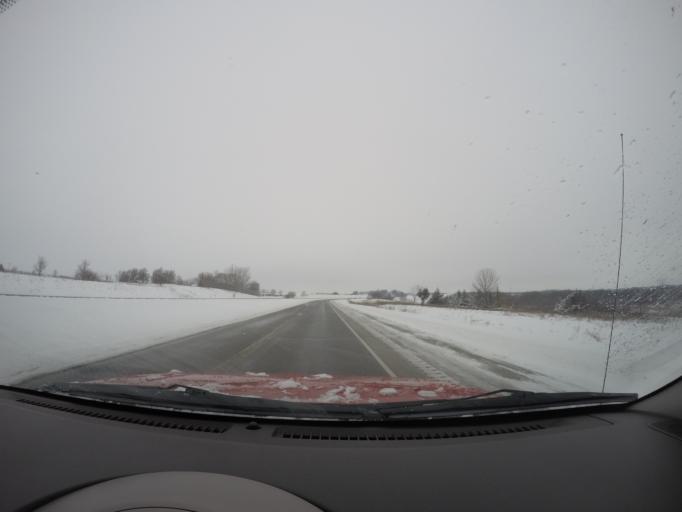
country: US
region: Minnesota
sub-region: Winona County
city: Saint Charles
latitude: 43.9354
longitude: -92.0059
